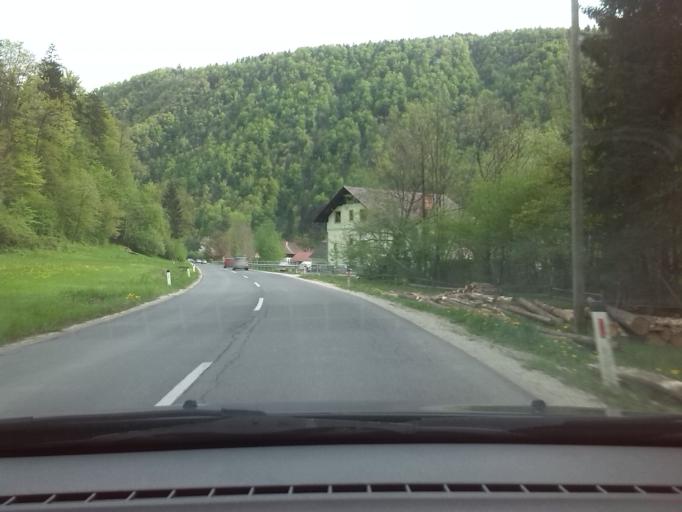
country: SI
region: Kamnik
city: Mekinje
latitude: 46.2298
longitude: 14.6672
